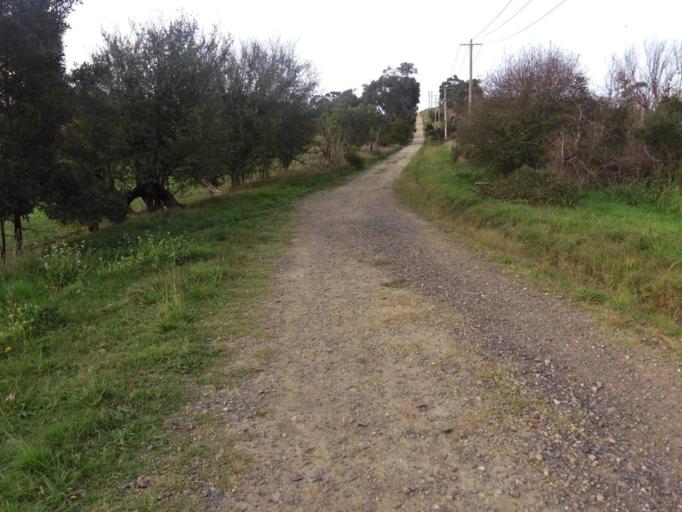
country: AU
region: Victoria
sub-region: Yarra Ranges
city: Belgrave South
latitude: -37.9229
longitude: 145.3222
